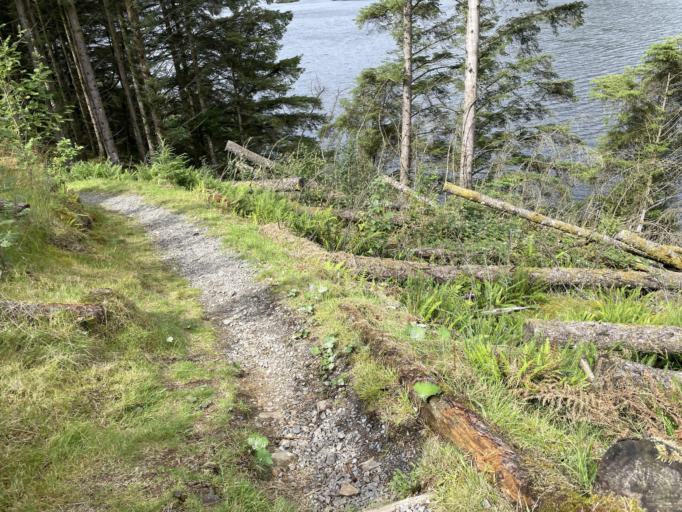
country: GB
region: Scotland
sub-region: Dumfries and Galloway
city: Newton Stewart
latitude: 55.0876
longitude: -4.4757
